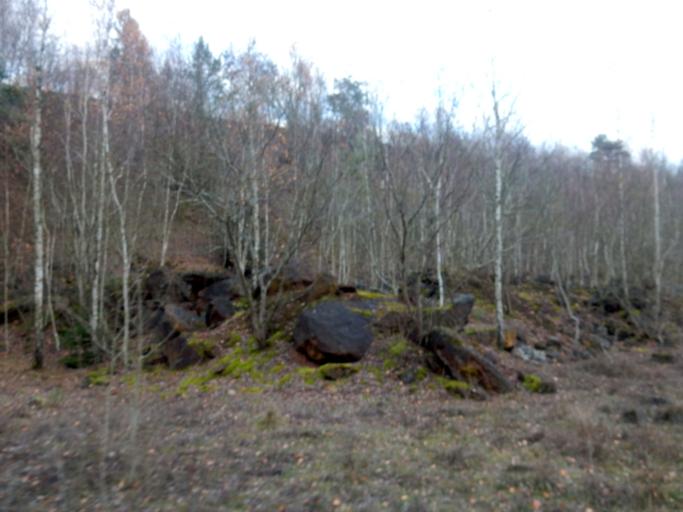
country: LU
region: Luxembourg
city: Tetange
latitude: 49.4809
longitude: 6.0635
